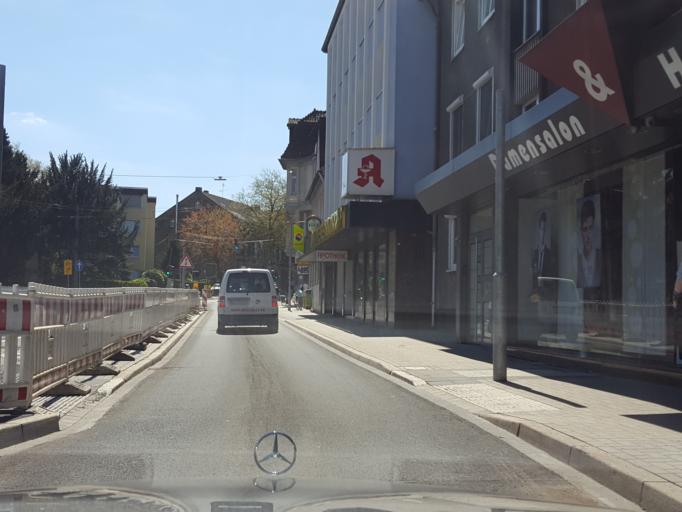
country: DE
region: North Rhine-Westphalia
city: Witten
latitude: 51.4736
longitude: 7.3244
